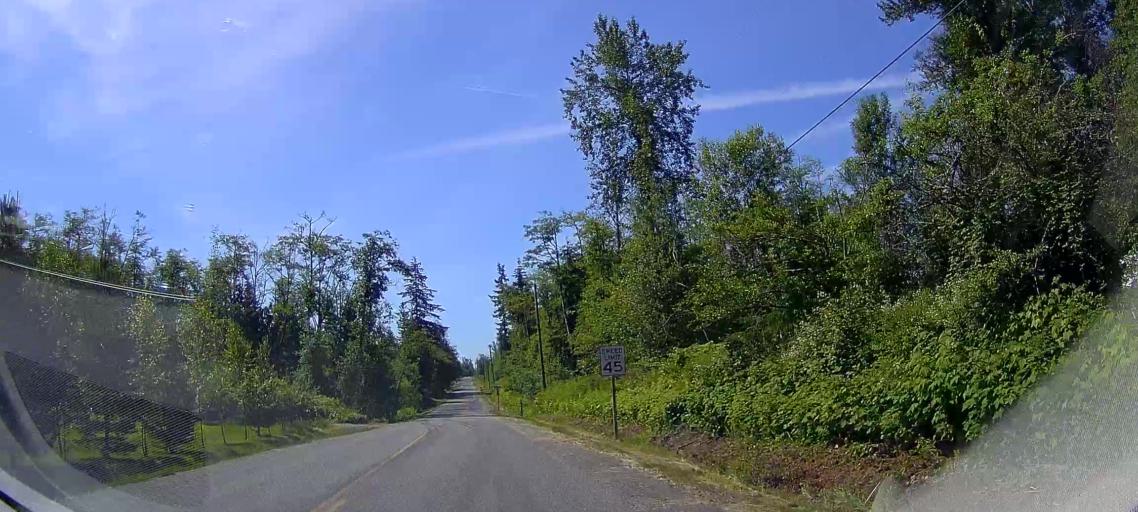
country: US
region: Washington
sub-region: Skagit County
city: Sedro-Woolley
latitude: 48.5424
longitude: -122.2486
